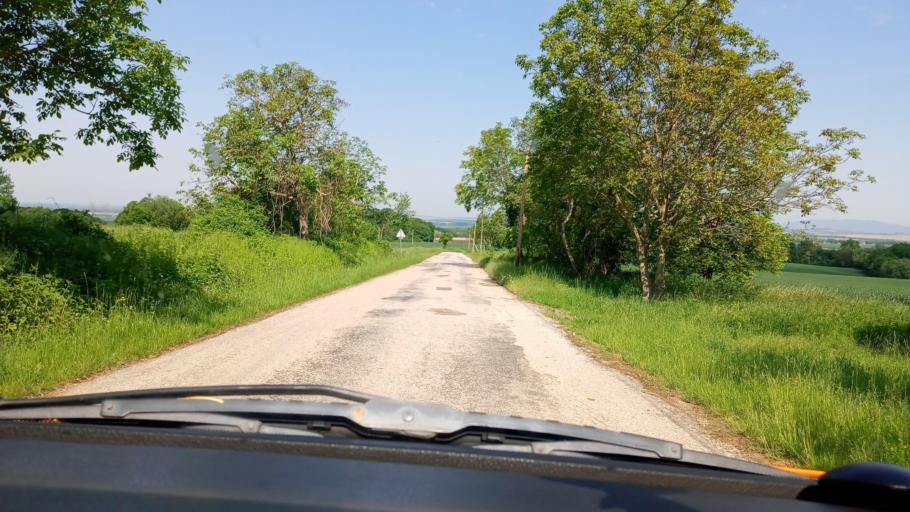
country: HU
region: Baranya
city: Harkany
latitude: 45.9053
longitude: 18.2498
